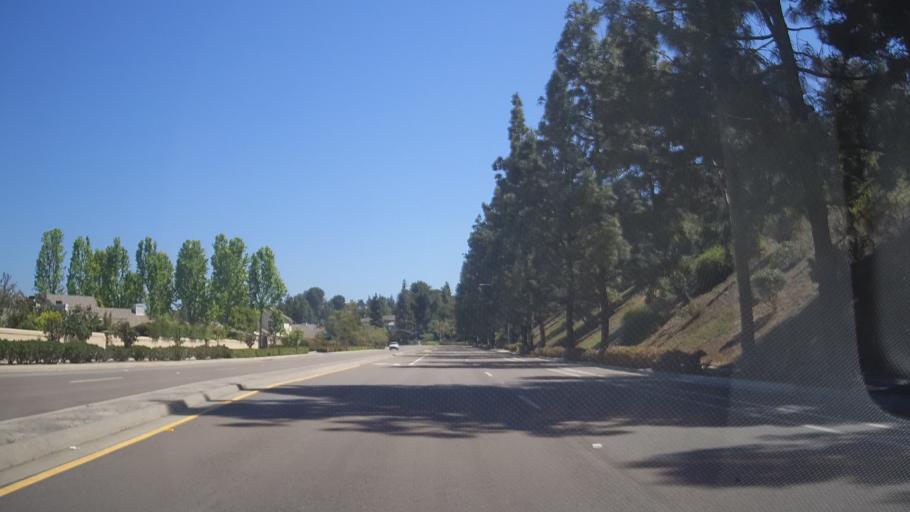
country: US
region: California
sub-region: San Diego County
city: Poway
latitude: 32.9695
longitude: -117.0882
